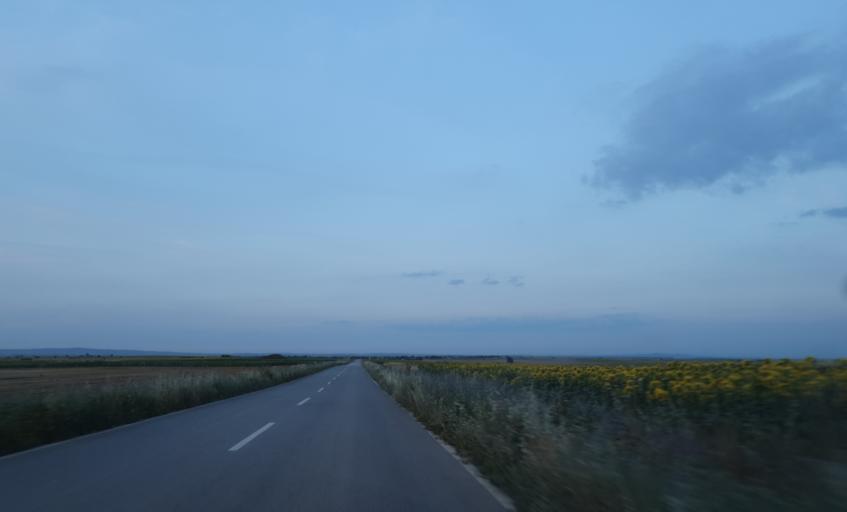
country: TR
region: Tekirdag
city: Beyazkoy
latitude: 41.4225
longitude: 27.6722
